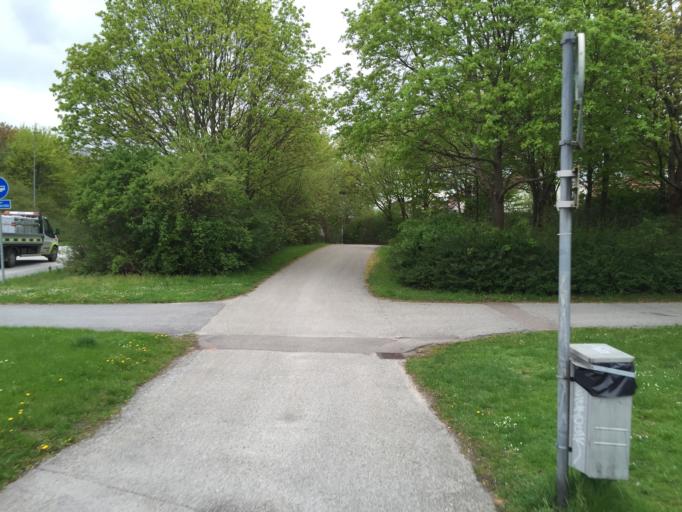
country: SE
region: Skane
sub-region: Lunds Kommun
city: Lund
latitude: 55.7204
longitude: 13.1622
